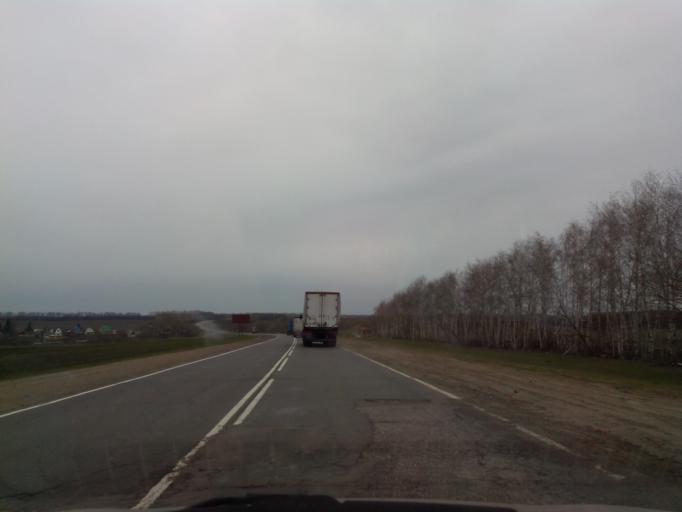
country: RU
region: Tambov
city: Pokrovo-Prigorodnoye
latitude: 52.6733
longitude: 41.3330
